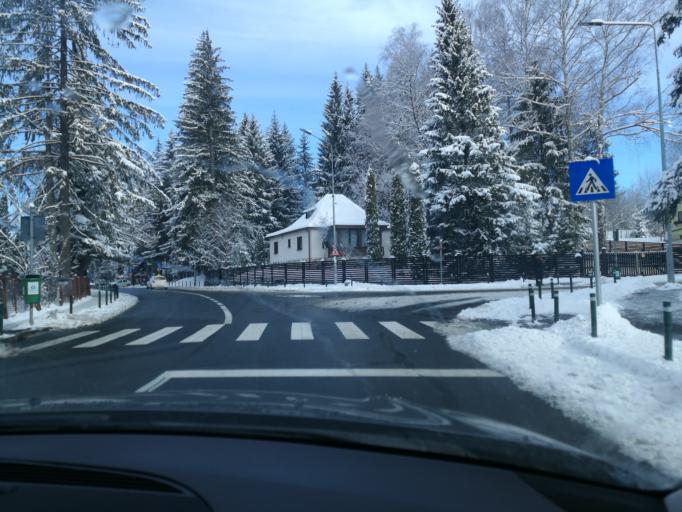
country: RO
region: Brasov
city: Brasov
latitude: 45.5941
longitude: 25.5537
